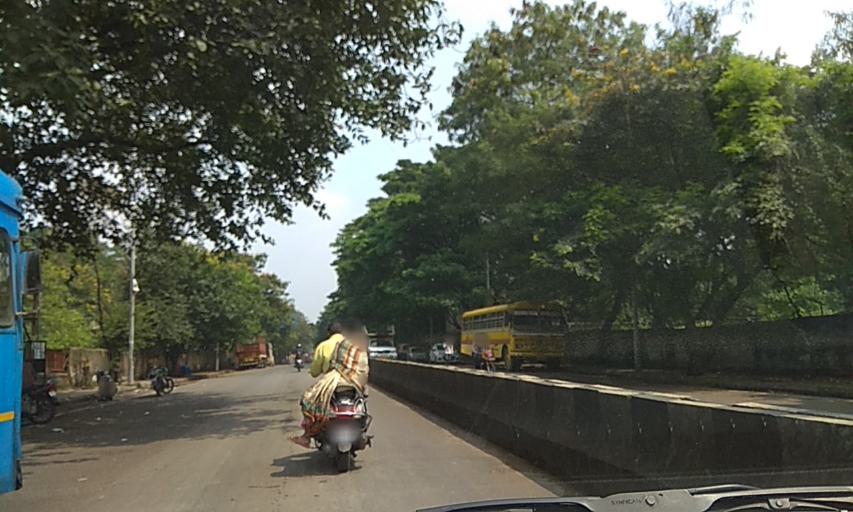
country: IN
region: Maharashtra
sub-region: Pune Division
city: Shivaji Nagar
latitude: 18.5372
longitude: 73.7943
